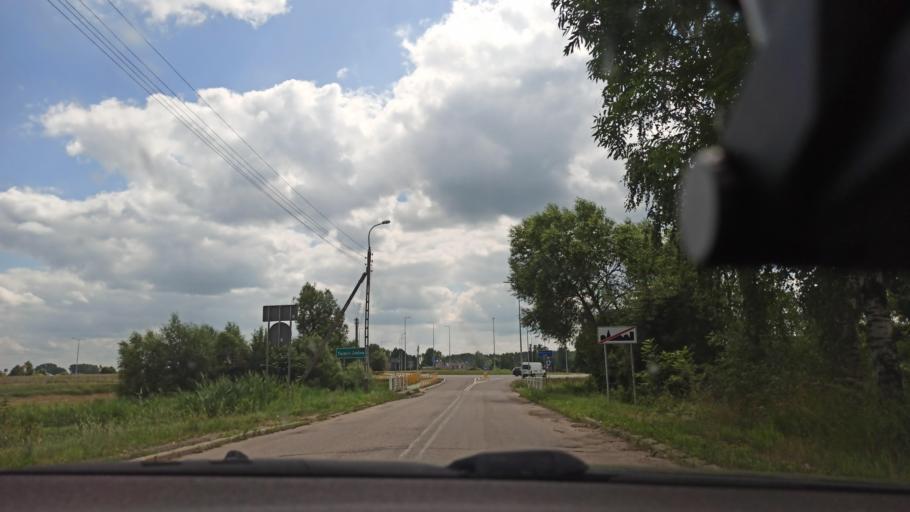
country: PL
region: Podlasie
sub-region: Powiat bialostocki
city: Turosn Koscielna
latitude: 53.0178
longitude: 23.0024
